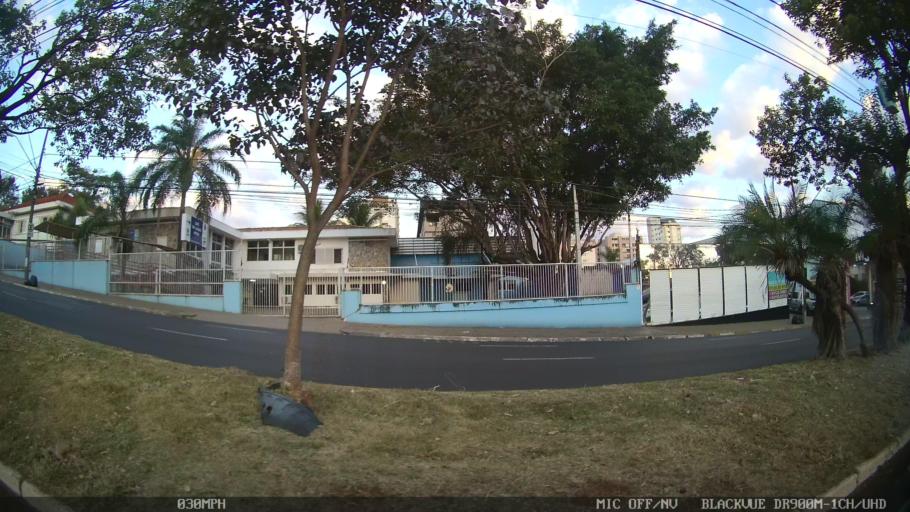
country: BR
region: Sao Paulo
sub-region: Ribeirao Preto
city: Ribeirao Preto
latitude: -21.1761
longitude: -47.7971
